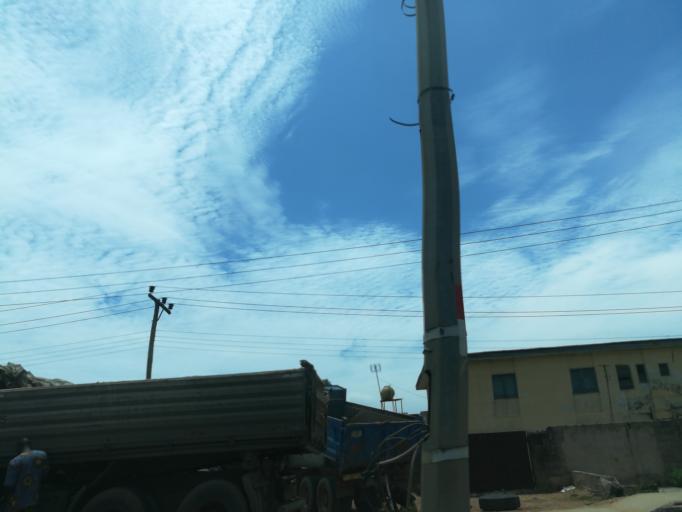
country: NG
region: Lagos
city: Ebute Ikorodu
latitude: 6.5977
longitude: 3.4935
